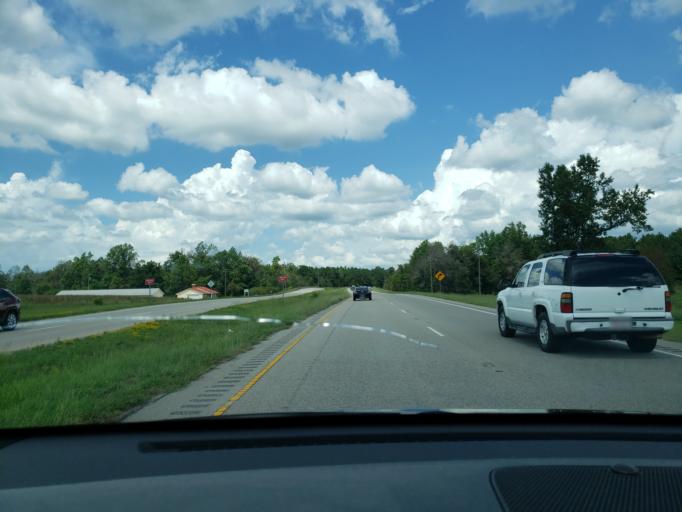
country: US
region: North Carolina
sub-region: Bladen County
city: Elizabethtown
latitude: 34.6761
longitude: -78.7402
